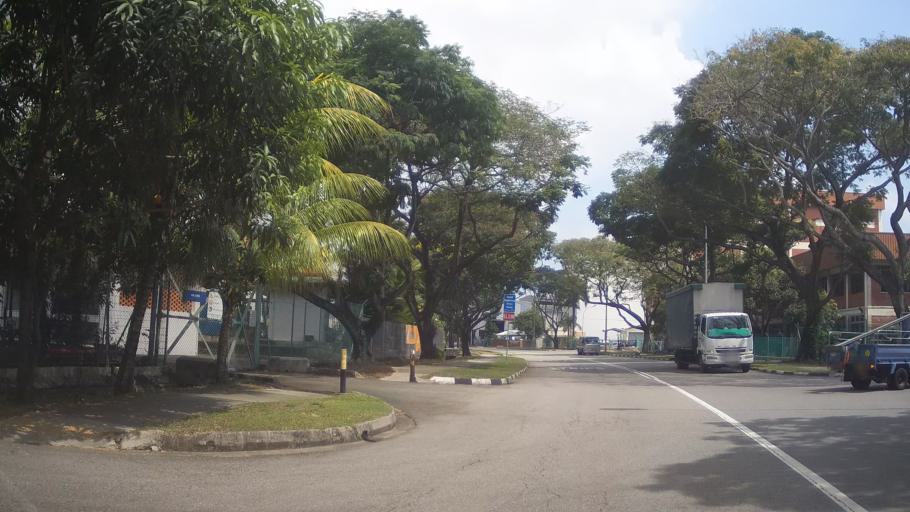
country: MY
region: Johor
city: Johor Bahru
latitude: 1.3101
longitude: 103.6630
